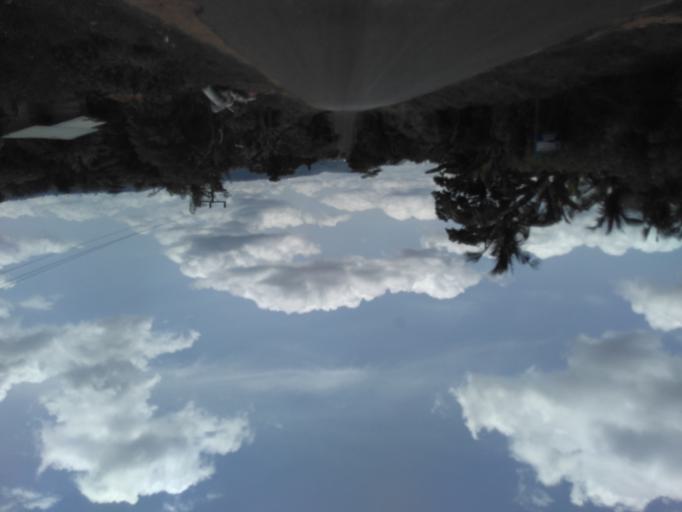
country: GH
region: Eastern
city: Koforidua
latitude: 6.1210
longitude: -0.1541
